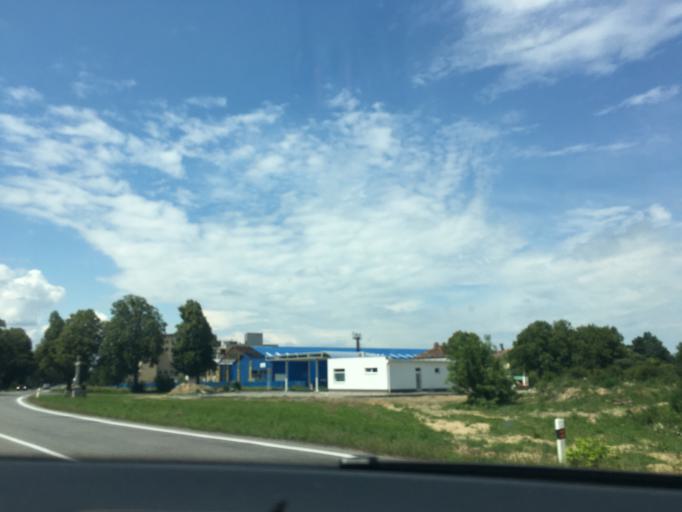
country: SK
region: Presovsky
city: Vranov nad Topl'ou
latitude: 48.8573
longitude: 21.7258
